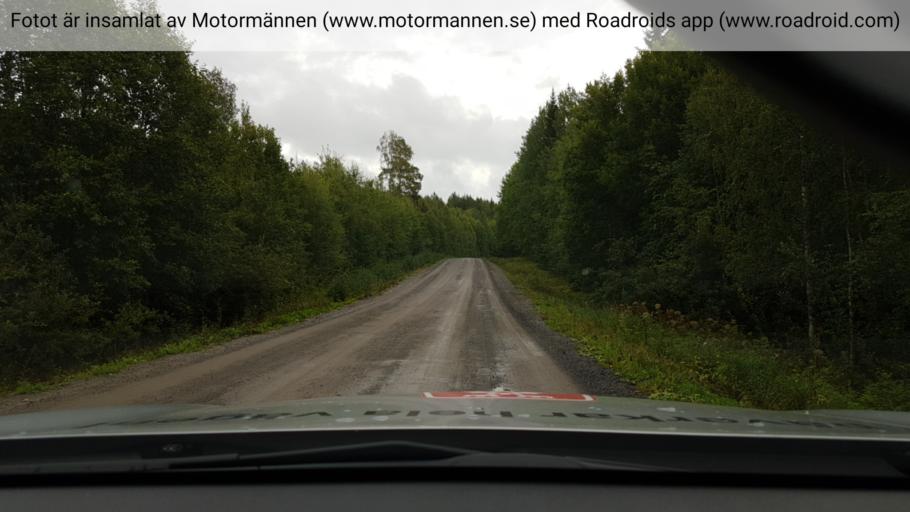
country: SE
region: Vaesterbotten
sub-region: Skelleftea Kommun
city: Burtraesk
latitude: 64.3484
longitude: 20.5284
